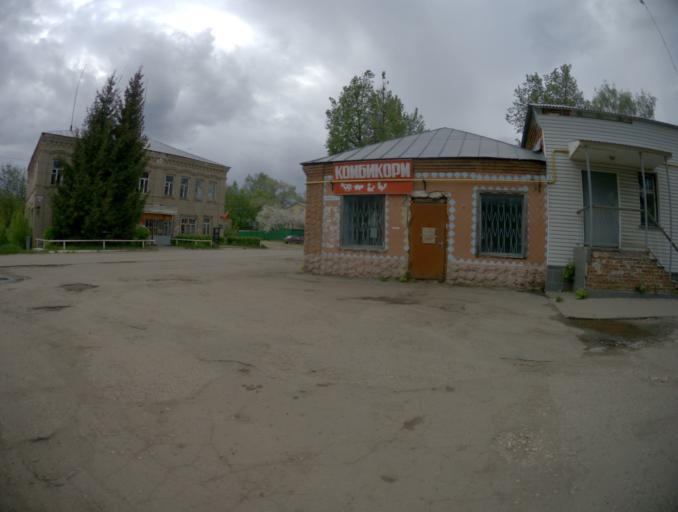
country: RU
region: Rjazan
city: Spas-Klepiki
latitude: 55.1282
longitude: 40.1701
